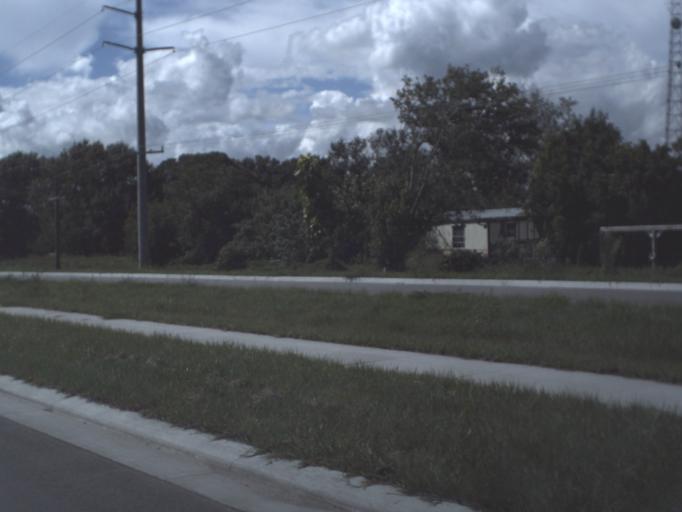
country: US
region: Florida
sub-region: Okeechobee County
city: Cypress Quarters
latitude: 27.2513
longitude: -80.7843
